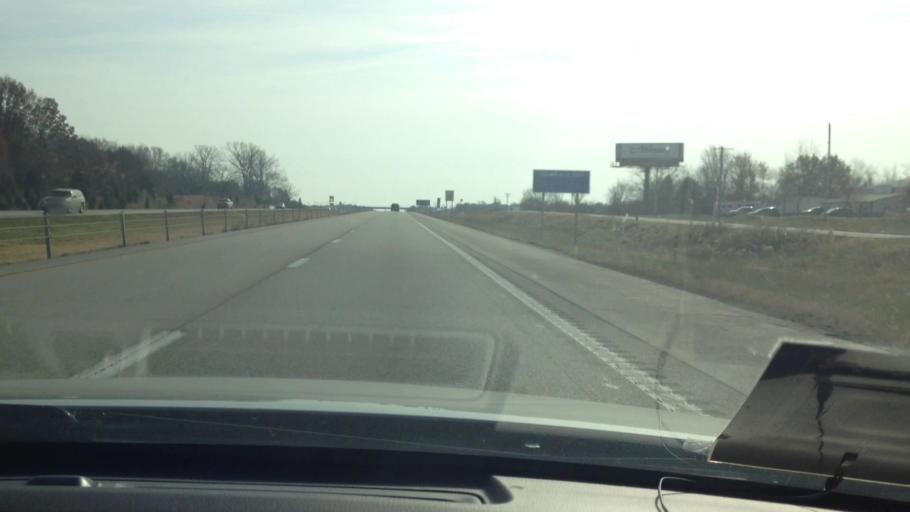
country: US
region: Missouri
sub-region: Cass County
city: Peculiar
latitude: 38.7323
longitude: -94.4648
